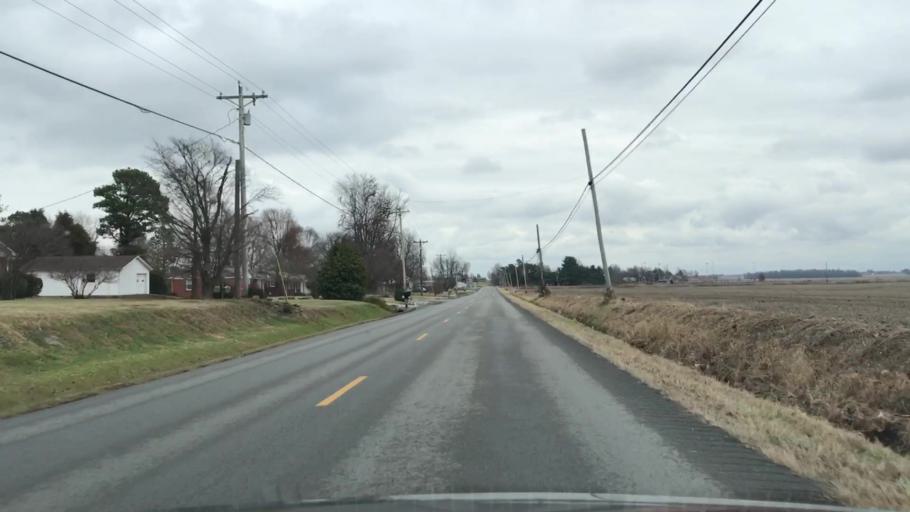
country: US
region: Kentucky
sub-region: McLean County
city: Calhoun
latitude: 37.5501
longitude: -87.2459
